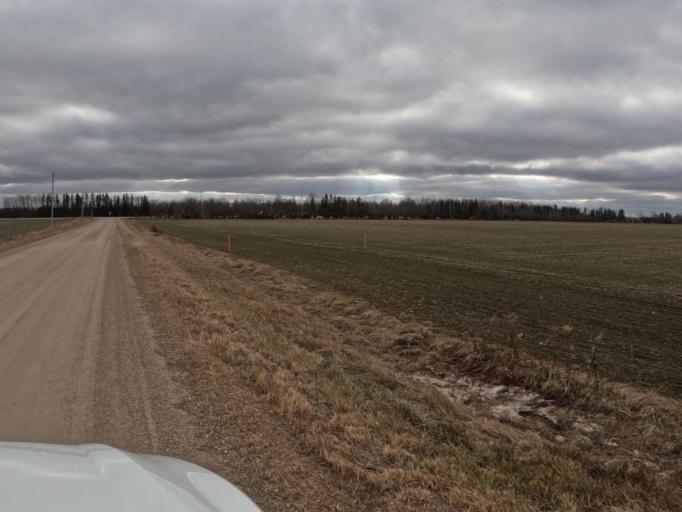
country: CA
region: Ontario
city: Shelburne
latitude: 43.8586
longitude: -80.3993
